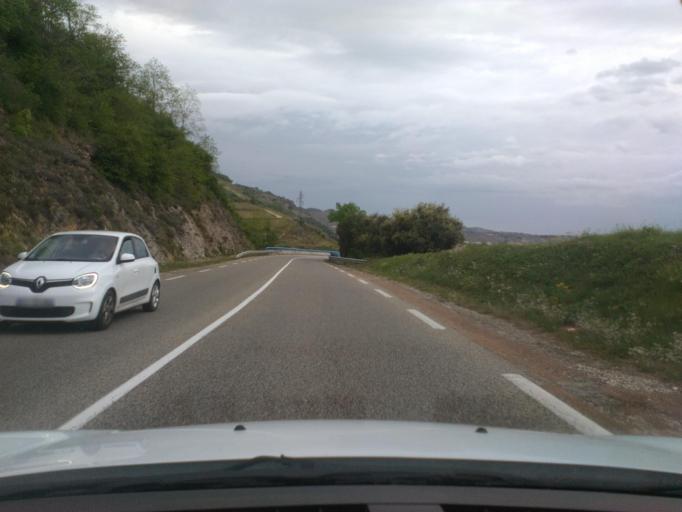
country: FR
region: Rhone-Alpes
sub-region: Departement de l'Ardeche
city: Mauves
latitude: 45.0413
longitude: 4.8270
